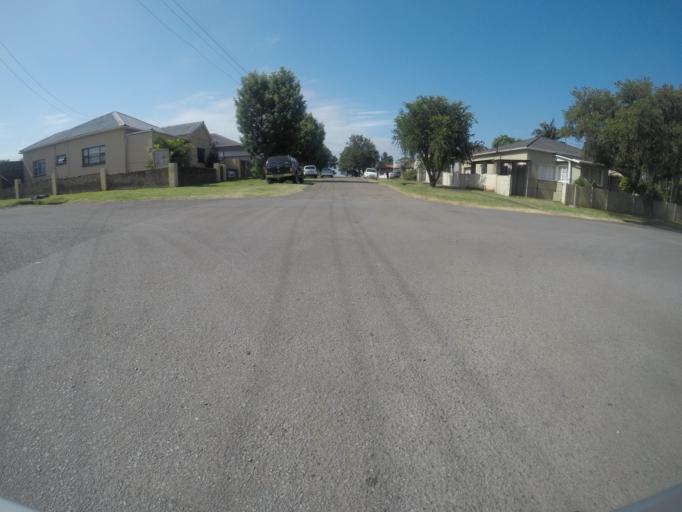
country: ZA
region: Eastern Cape
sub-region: Buffalo City Metropolitan Municipality
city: East London
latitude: -32.9696
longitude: 27.8778
